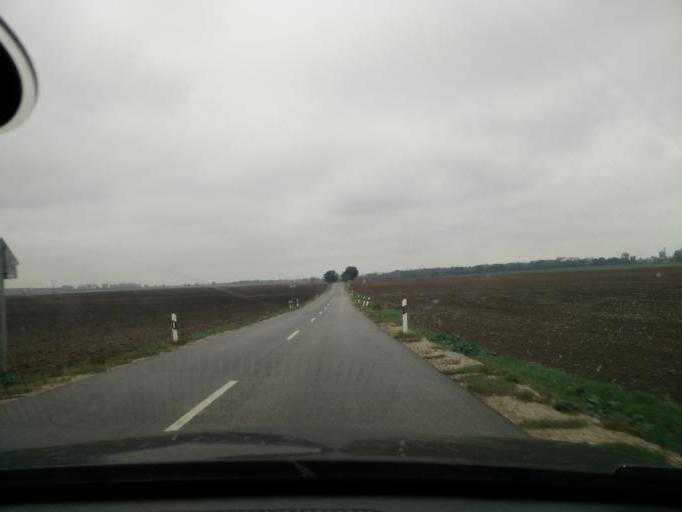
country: HU
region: Komarom-Esztergom
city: Bajna
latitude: 47.6457
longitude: 18.5743
